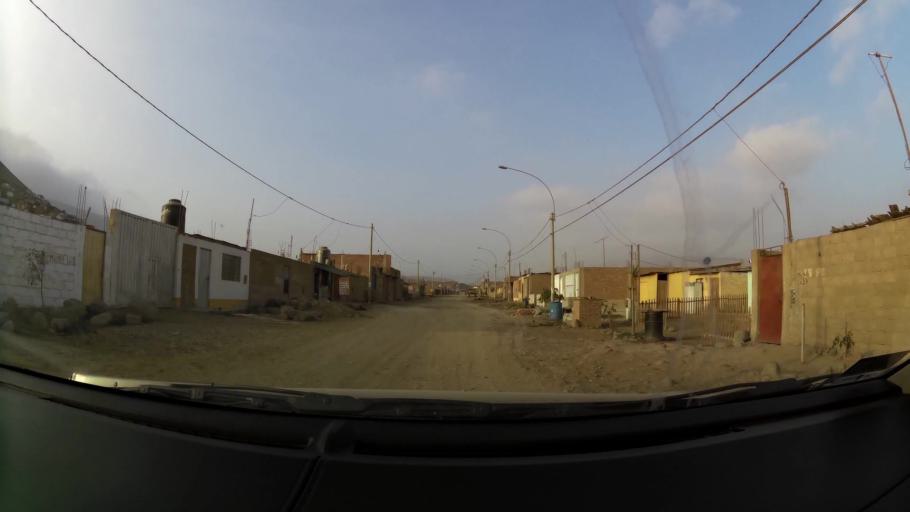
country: PE
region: Lima
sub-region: Lima
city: Santa Rosa
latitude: -11.7442
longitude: -77.1472
